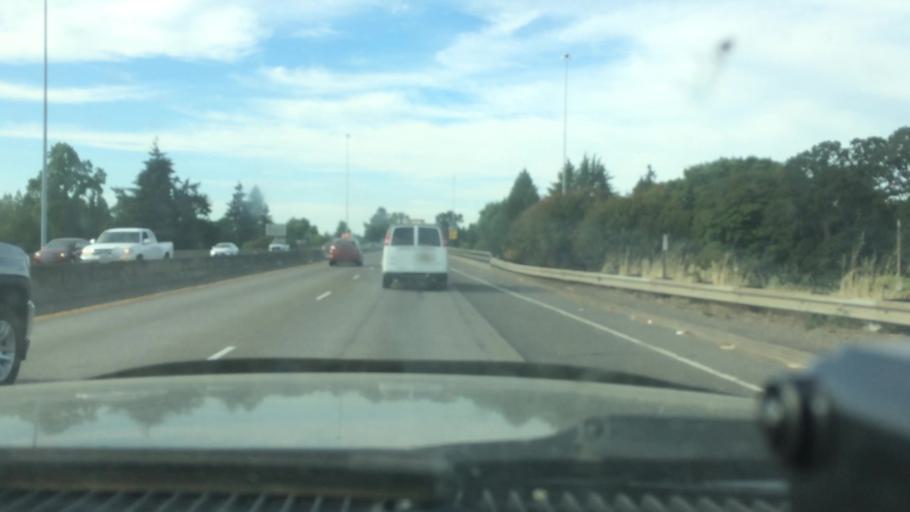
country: US
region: Oregon
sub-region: Lane County
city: Eugene
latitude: 44.0605
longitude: -123.1010
